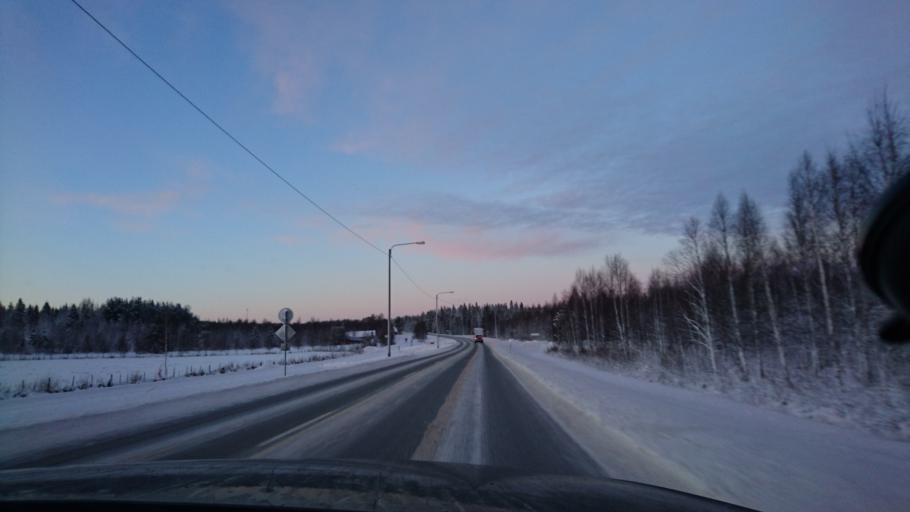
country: FI
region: Lapland
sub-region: Rovaniemi
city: Ranua
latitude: 65.9362
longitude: 26.4911
